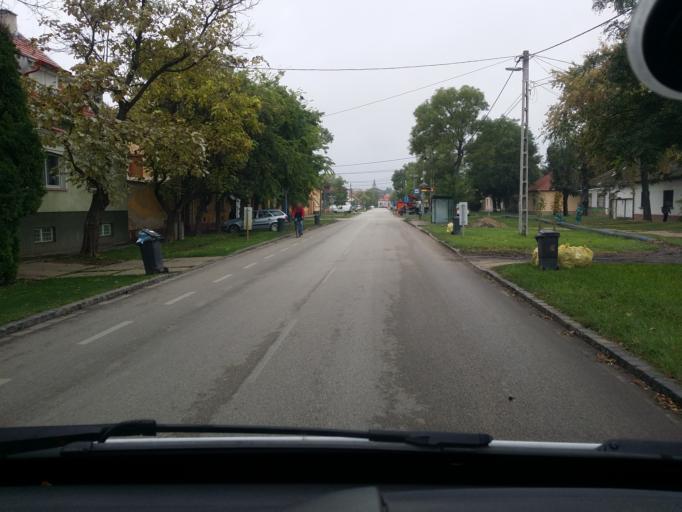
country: HU
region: Bacs-Kiskun
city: Kecskemet
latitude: 46.8973
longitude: 19.6982
